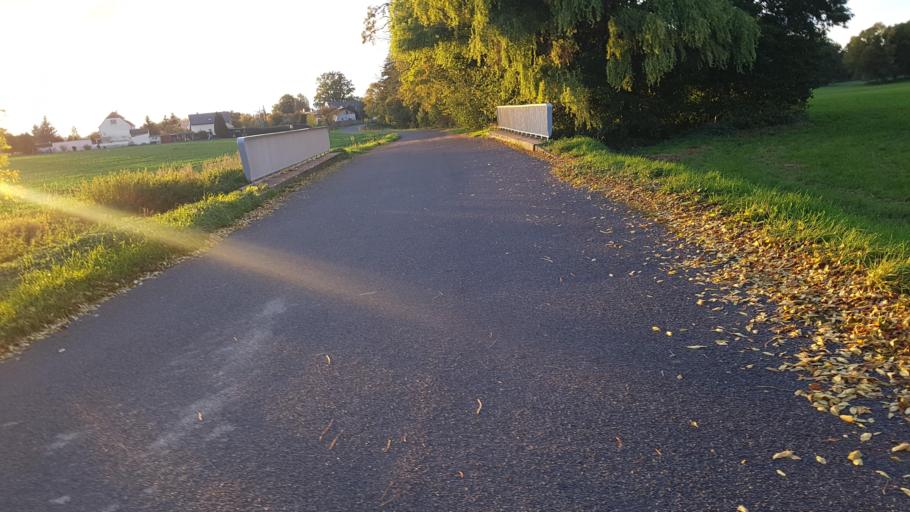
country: DE
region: Saxony
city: Priestewitz
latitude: 51.2318
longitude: 13.5402
